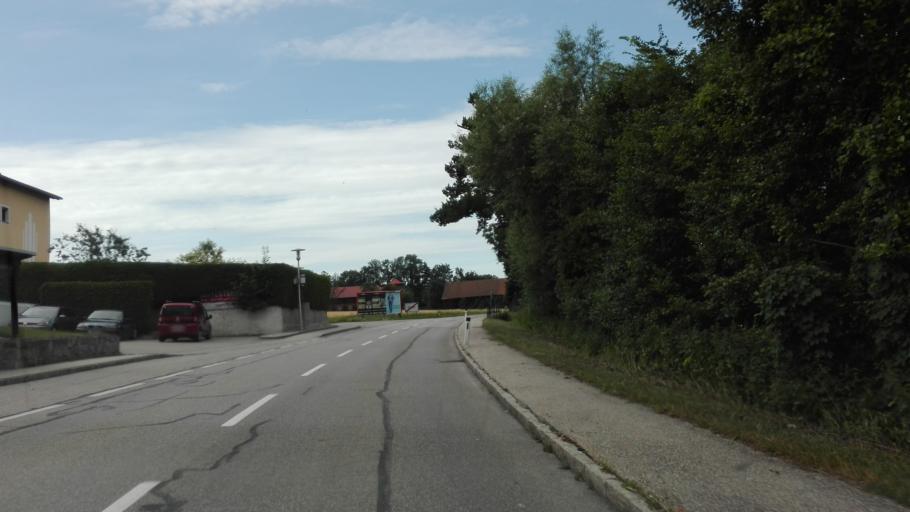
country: AT
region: Upper Austria
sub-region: Politischer Bezirk Grieskirchen
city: Grieskirchen
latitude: 48.2473
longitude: 13.8126
